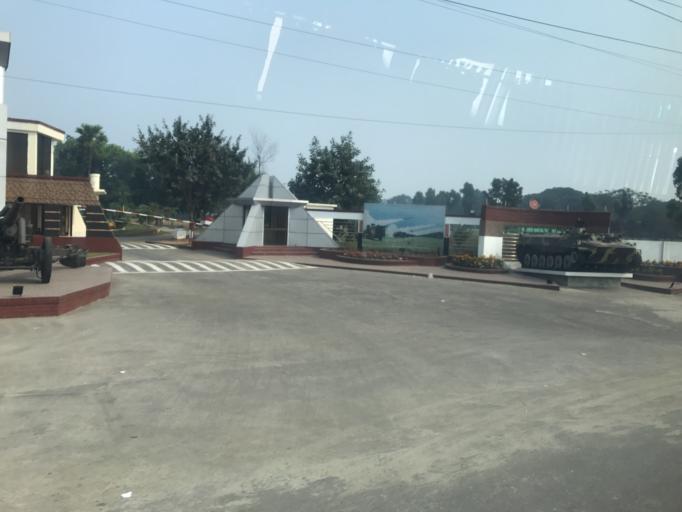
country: BD
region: Dhaka
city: Tungi
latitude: 23.9058
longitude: 90.2669
